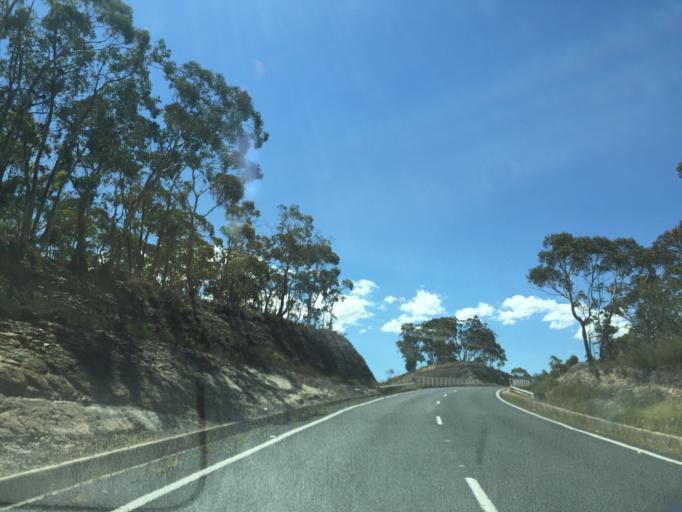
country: AU
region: New South Wales
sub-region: Lithgow
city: Lithgow
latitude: -33.4284
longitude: 150.1047
